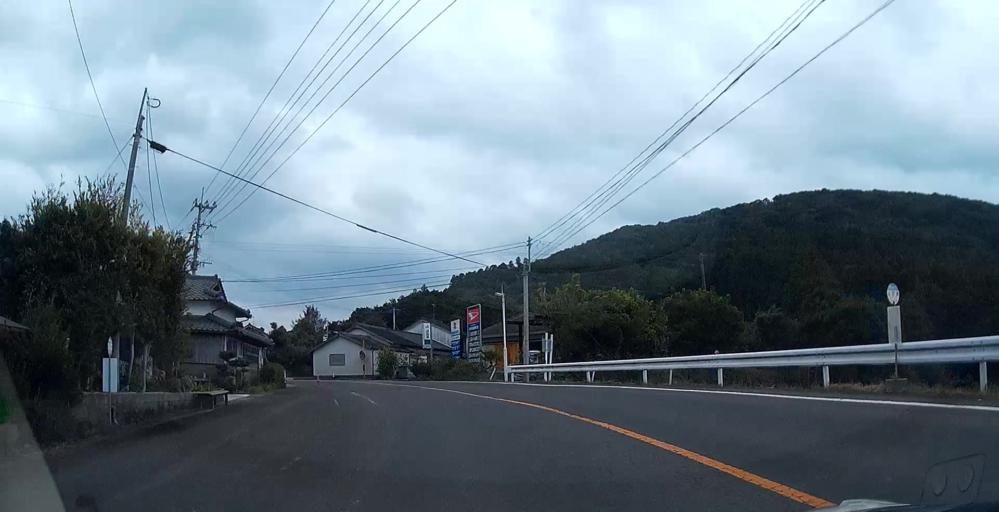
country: JP
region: Kagoshima
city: Akune
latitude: 32.0990
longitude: 130.1534
